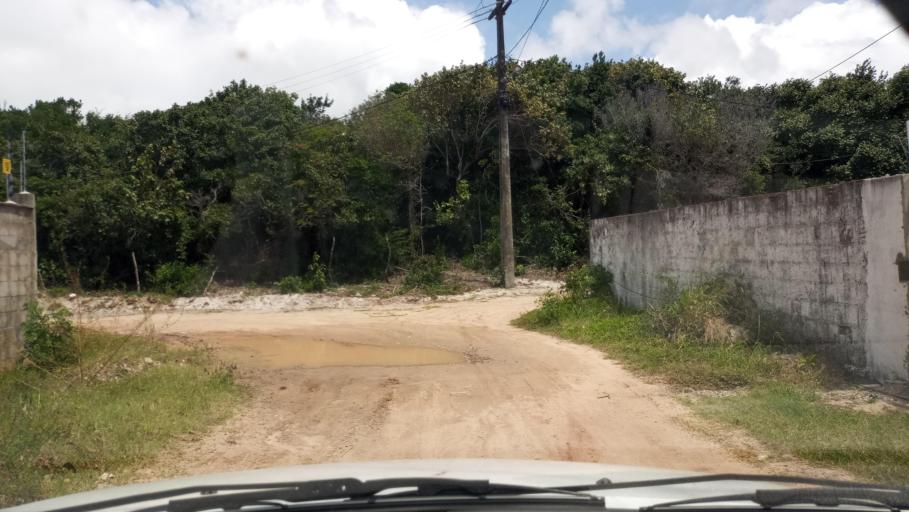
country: BR
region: Rio Grande do Norte
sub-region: Ares
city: Ares
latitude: -6.2461
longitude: -35.0445
